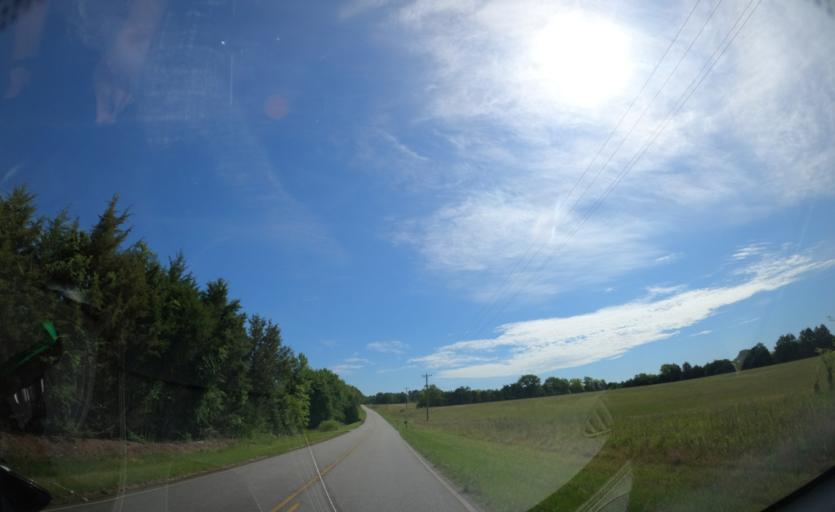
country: US
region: Georgia
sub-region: Elbert County
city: Elberton
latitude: 34.0773
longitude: -82.7388
